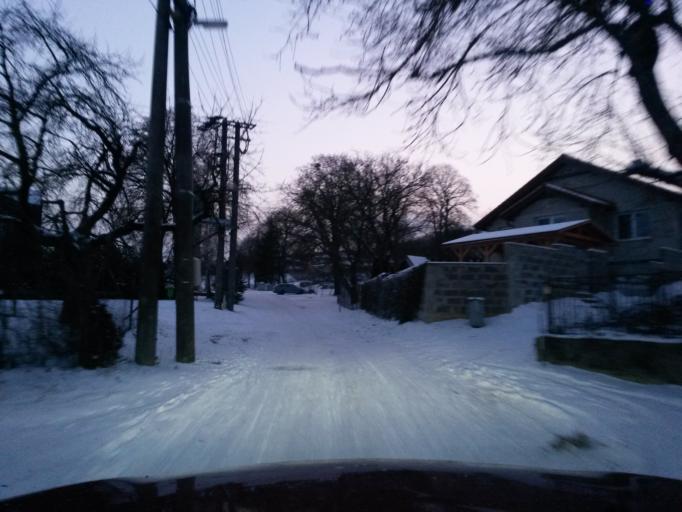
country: SK
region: Kosicky
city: Kosice
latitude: 48.7451
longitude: 21.3194
